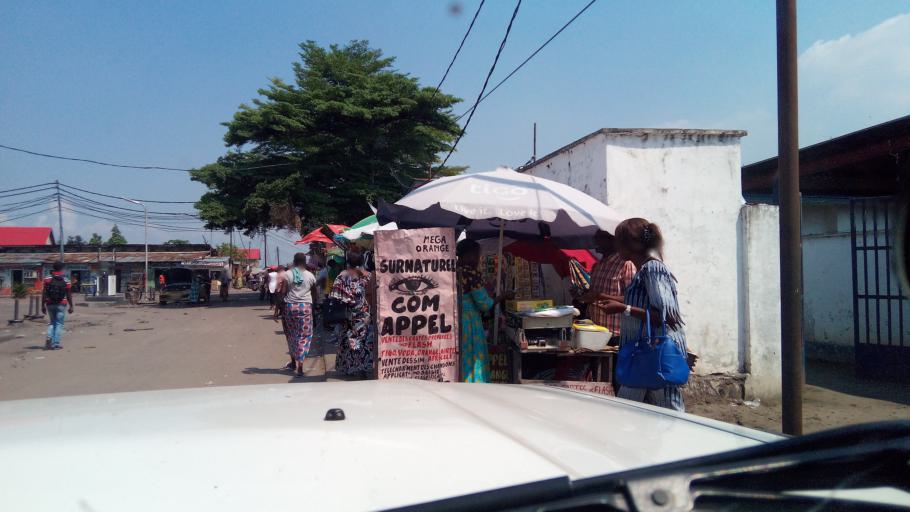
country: CD
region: Kinshasa
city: Kinshasa
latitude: -4.3691
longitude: 15.2973
